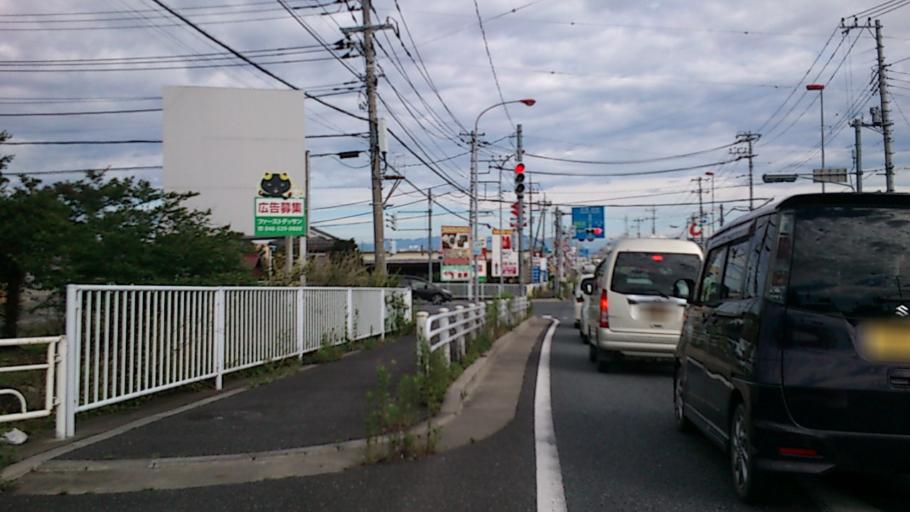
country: JP
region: Saitama
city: Honjo
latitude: 36.2310
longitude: 139.2131
